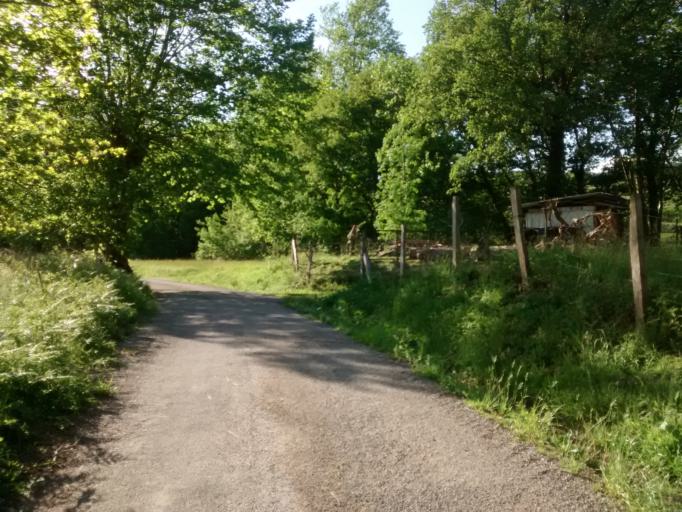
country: ES
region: Cantabria
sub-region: Provincia de Cantabria
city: Entrambasaguas
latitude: 43.3382
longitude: -3.6628
